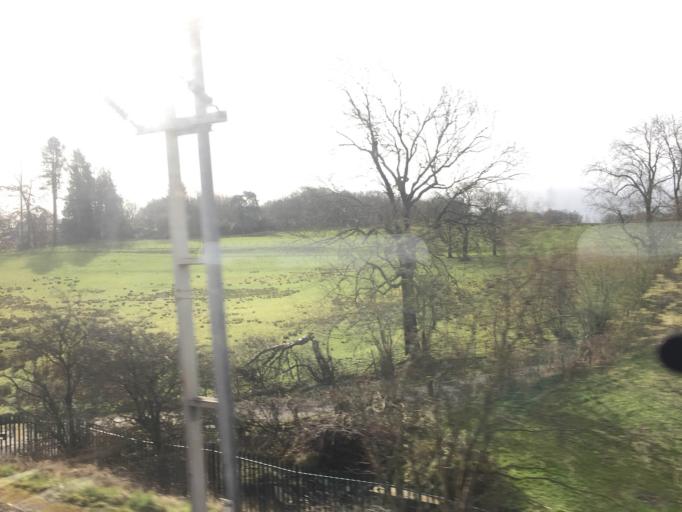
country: GB
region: England
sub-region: Cumbria
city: Kendal
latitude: 54.3595
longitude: -2.6409
